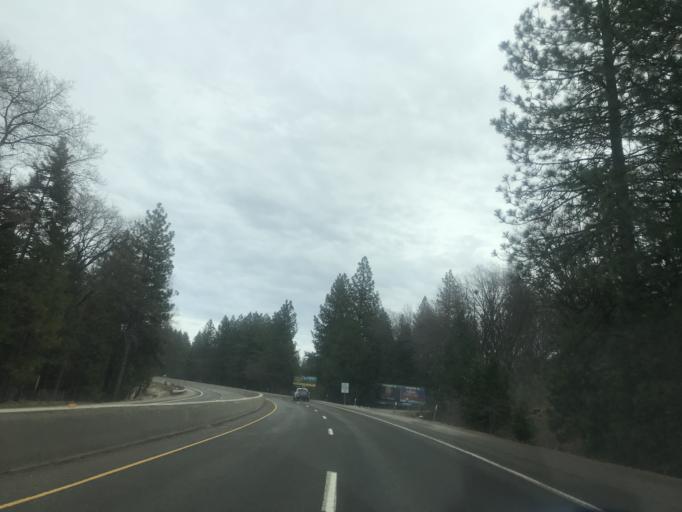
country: US
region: California
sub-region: El Dorado County
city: Camino
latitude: 38.7342
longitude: -120.6713
